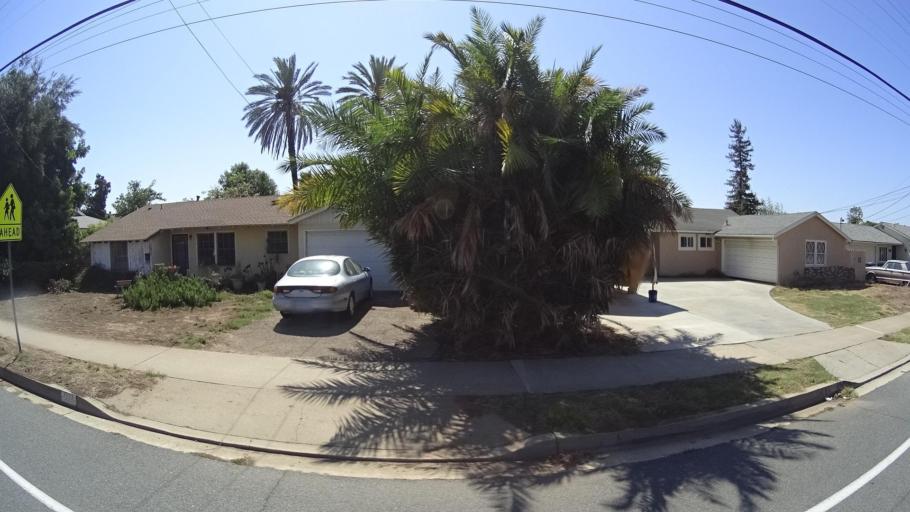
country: US
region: California
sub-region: San Diego County
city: Bostonia
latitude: 32.8002
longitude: -116.9242
